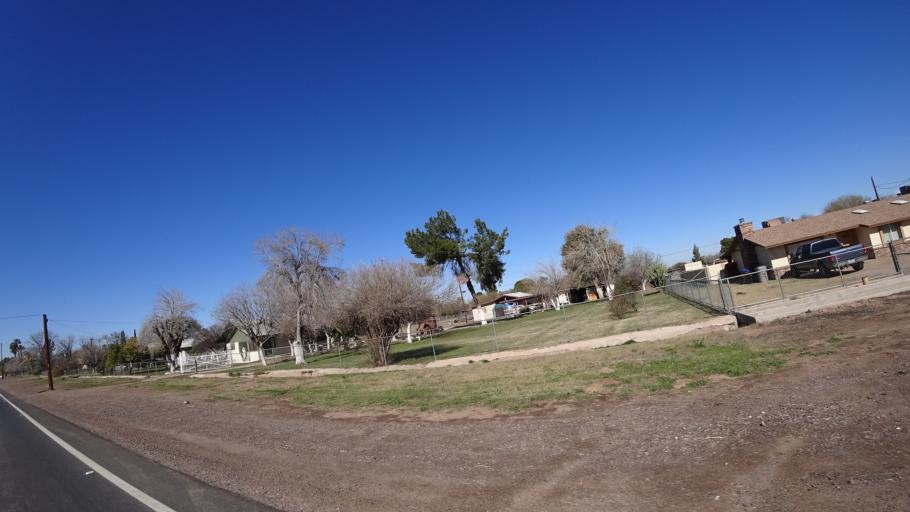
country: US
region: Arizona
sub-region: Maricopa County
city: Avondale
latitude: 33.3918
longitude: -112.3013
